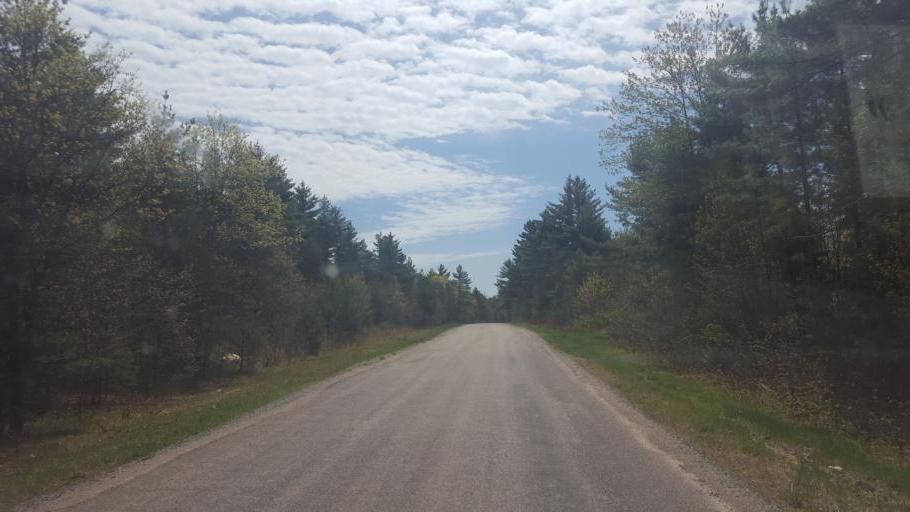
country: US
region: Wisconsin
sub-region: Clark County
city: Neillsville
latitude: 44.3124
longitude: -90.5087
